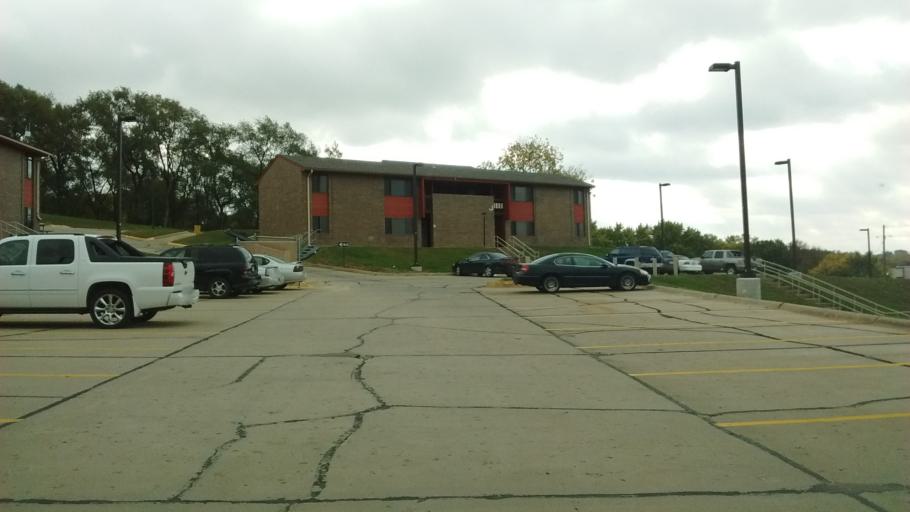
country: US
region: Iowa
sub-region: Woodbury County
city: Sioux City
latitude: 42.4800
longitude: -96.3447
